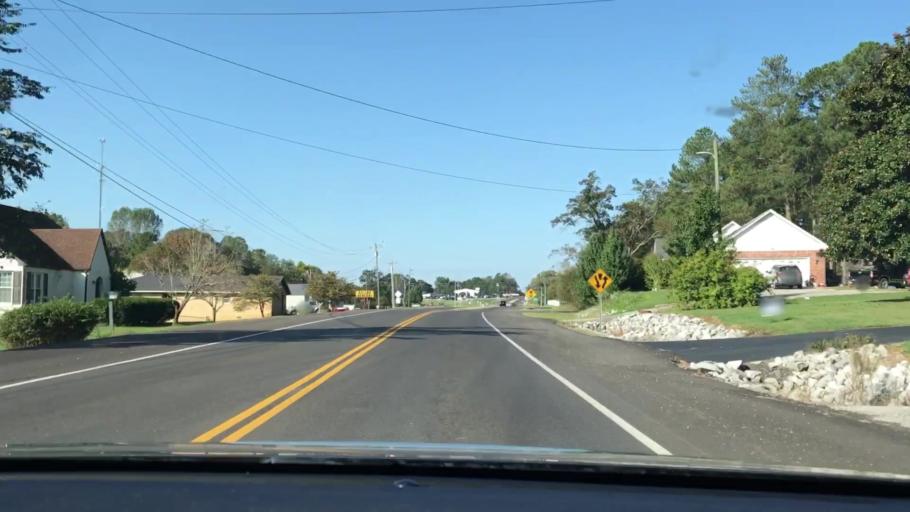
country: US
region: Kentucky
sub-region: Marshall County
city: Benton
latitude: 36.7660
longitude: -88.3066
